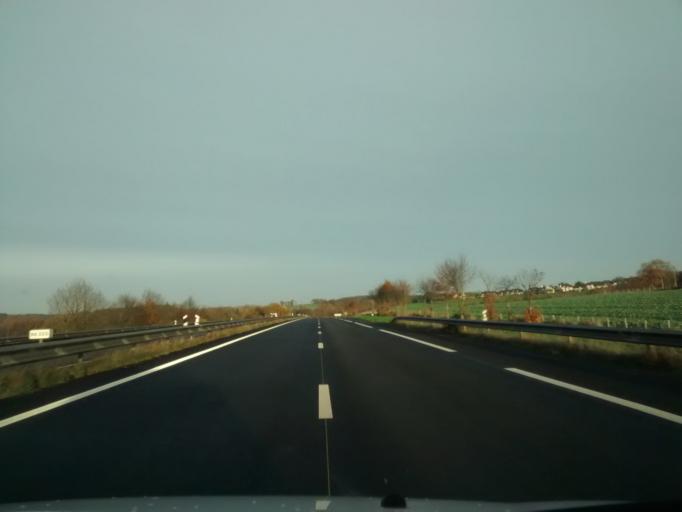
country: FR
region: Brittany
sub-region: Departement d'Ille-et-Vilaine
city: Pleugueneuc
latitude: 48.3884
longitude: -1.9048
